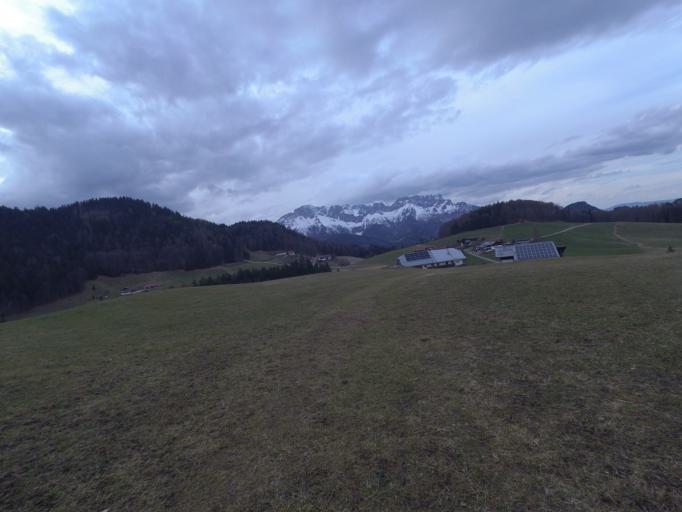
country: AT
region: Salzburg
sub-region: Politischer Bezirk Hallein
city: Hallein
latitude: 47.6623
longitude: 13.0797
